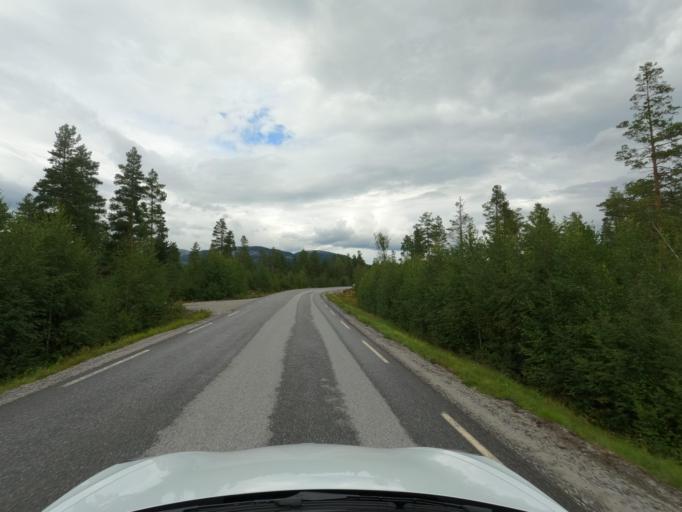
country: NO
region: Telemark
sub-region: Notodden
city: Notodden
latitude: 59.7114
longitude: 9.1524
